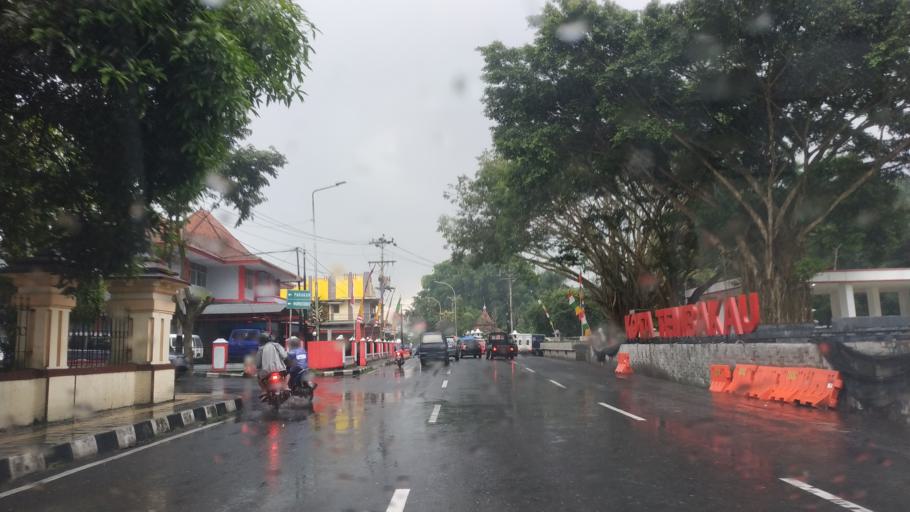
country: ID
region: Central Java
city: Magelang
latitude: -7.3163
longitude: 110.1749
